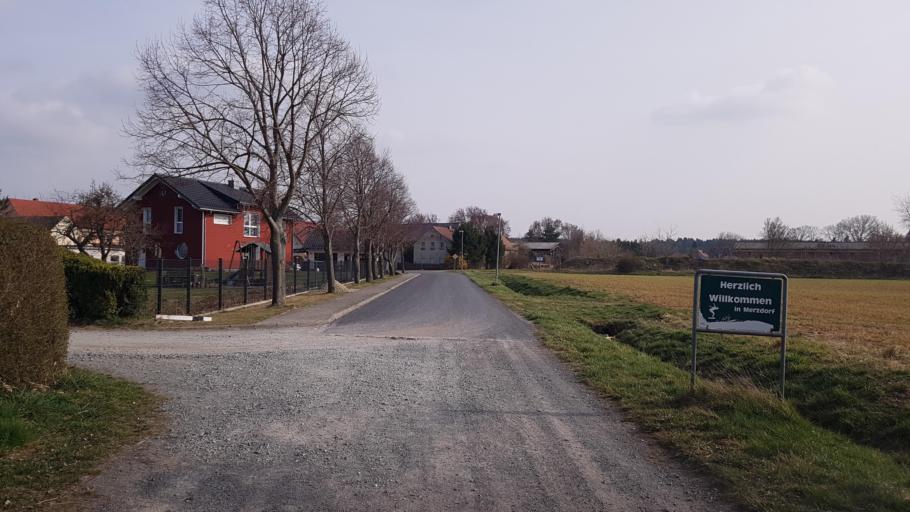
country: DE
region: Brandenburg
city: Merzdorf
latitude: 51.4071
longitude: 13.5316
